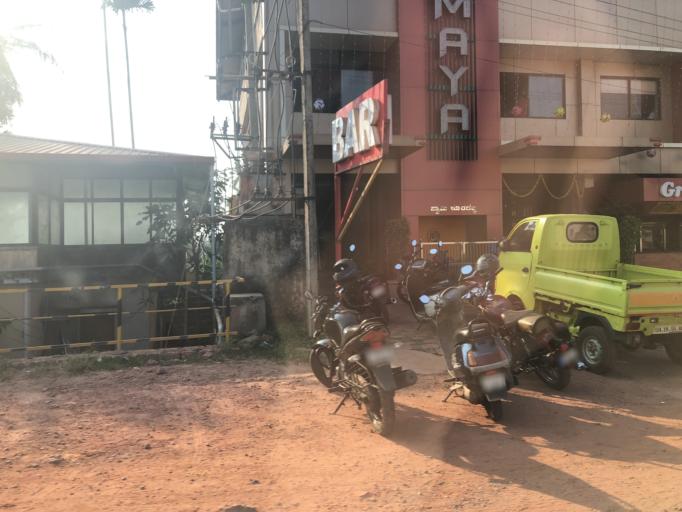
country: IN
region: Karnataka
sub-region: Dakshina Kannada
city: Ullal
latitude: 12.8155
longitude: 74.8585
